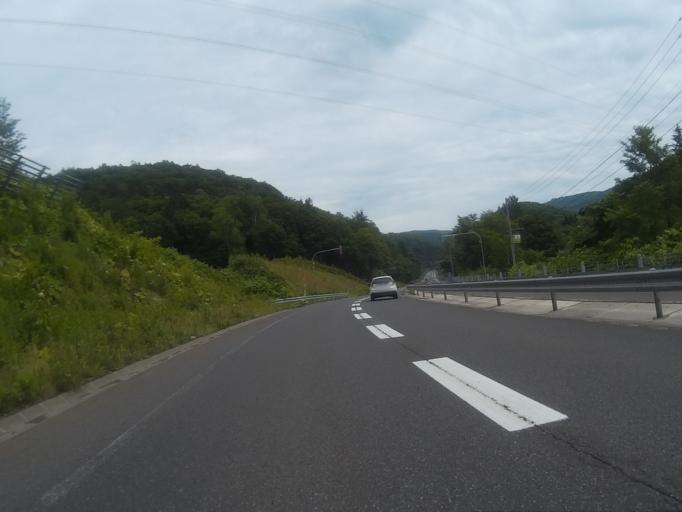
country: JP
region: Hokkaido
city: Otaru
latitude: 42.8495
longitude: 141.0409
